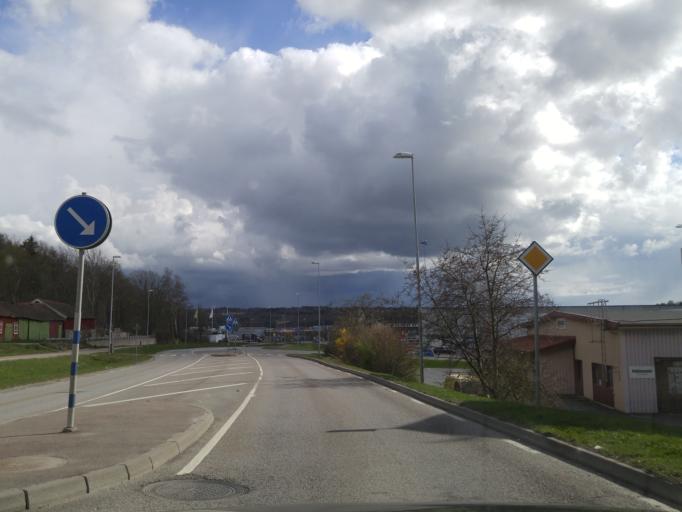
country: SE
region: Vaestra Goetaland
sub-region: Goteborg
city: Majorna
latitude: 57.6527
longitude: 11.9510
